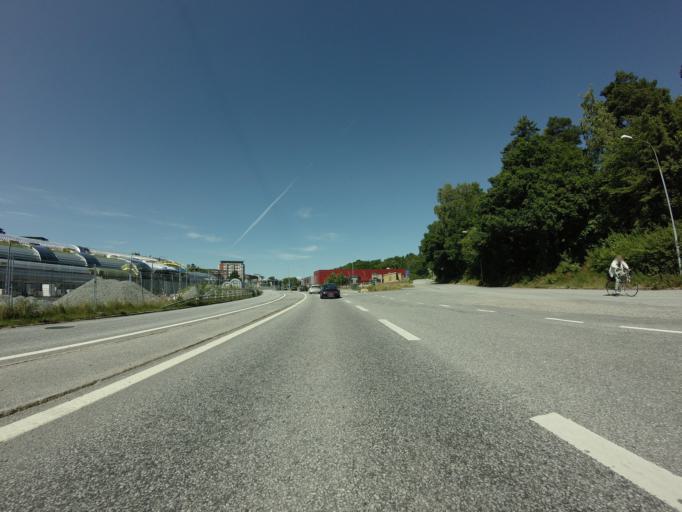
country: SE
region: Stockholm
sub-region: Lidingo
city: Lidingoe
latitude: 59.3473
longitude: 18.1549
